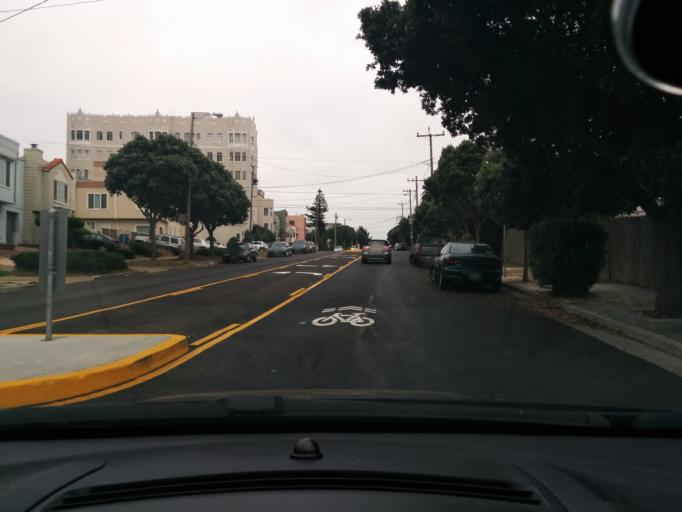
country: US
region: California
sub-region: Marin County
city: Sausalito
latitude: 37.7800
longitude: -122.5073
